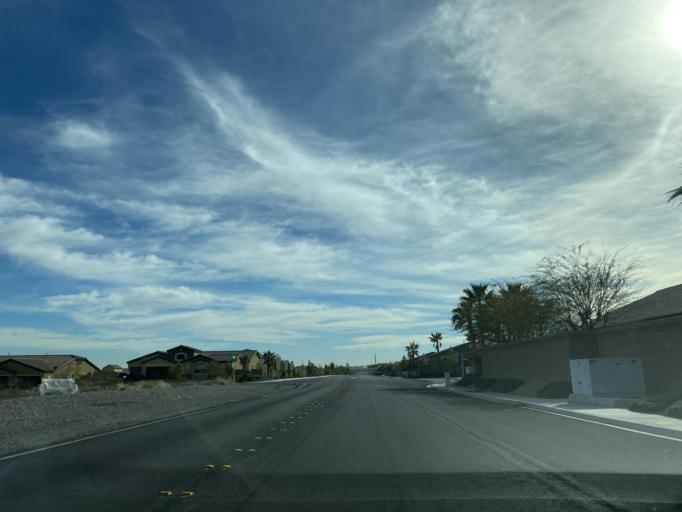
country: US
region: Nevada
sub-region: Clark County
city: Summerlin South
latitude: 36.2706
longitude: -115.3242
